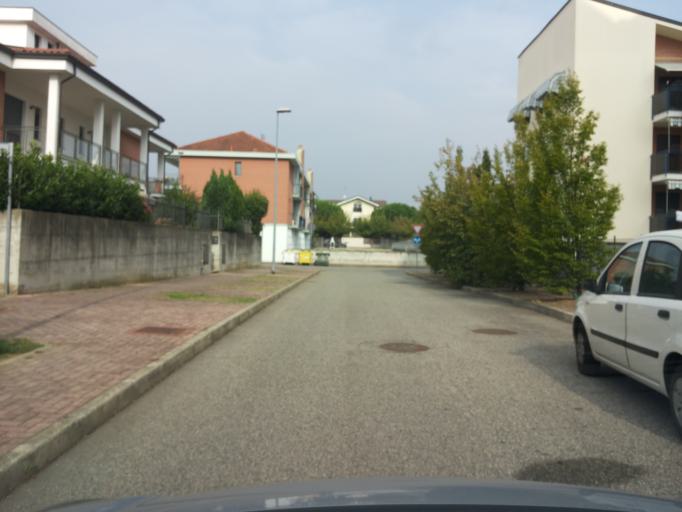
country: IT
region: Piedmont
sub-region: Provincia di Vercelli
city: Vercelli
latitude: 45.3128
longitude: 8.4340
